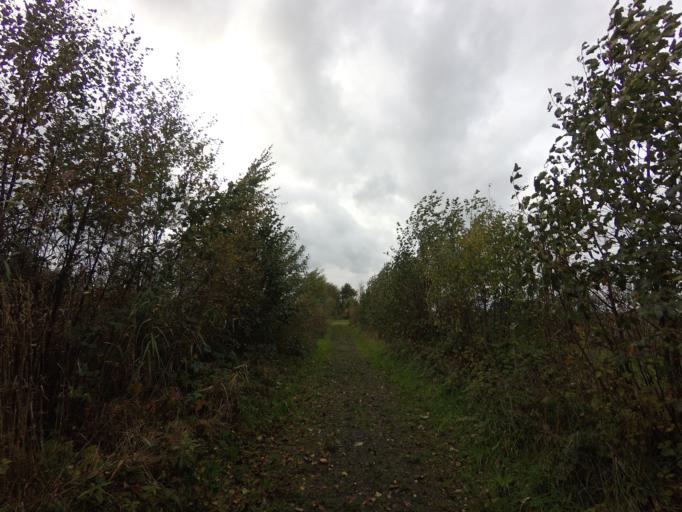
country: NL
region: Utrecht
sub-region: Stichtse Vecht
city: Breukelen
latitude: 52.2099
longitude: 4.9435
